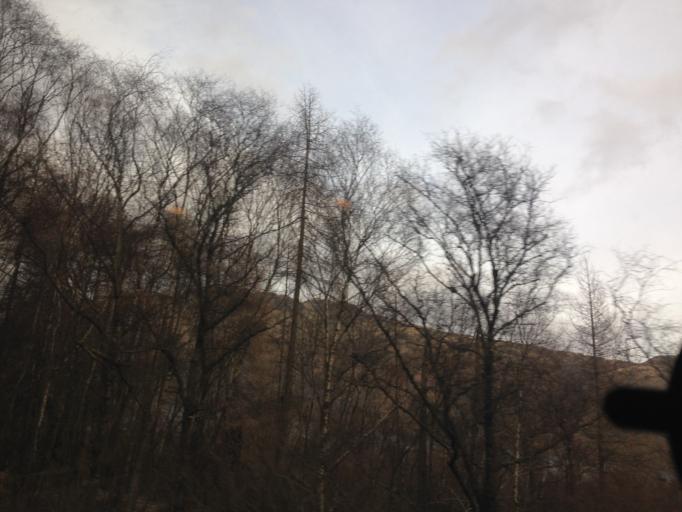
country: GB
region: Scotland
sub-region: Argyll and Bute
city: Garelochhead
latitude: 56.2156
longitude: -4.6987
